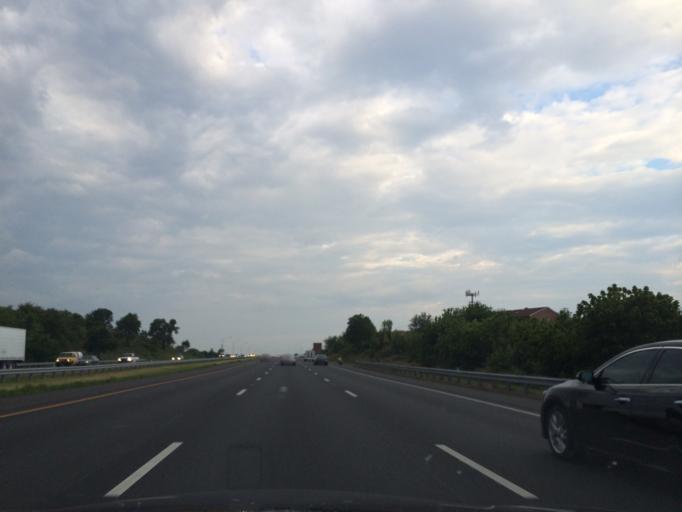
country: US
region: Maryland
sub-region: Frederick County
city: Bartonsville
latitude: 39.4042
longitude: -77.3692
